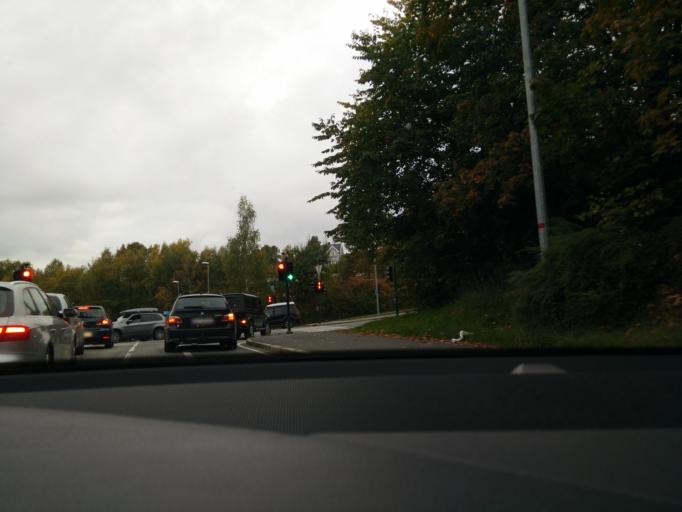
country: NO
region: Akershus
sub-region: Baerum
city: Lysaker
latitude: 59.9272
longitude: 10.6217
